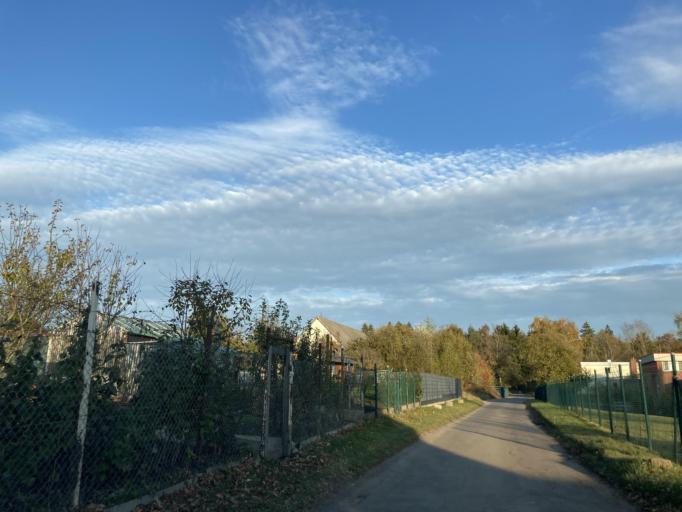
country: DE
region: Baden-Wuerttemberg
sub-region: Freiburg Region
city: Villingen-Schwenningen
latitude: 48.0428
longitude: 8.4668
